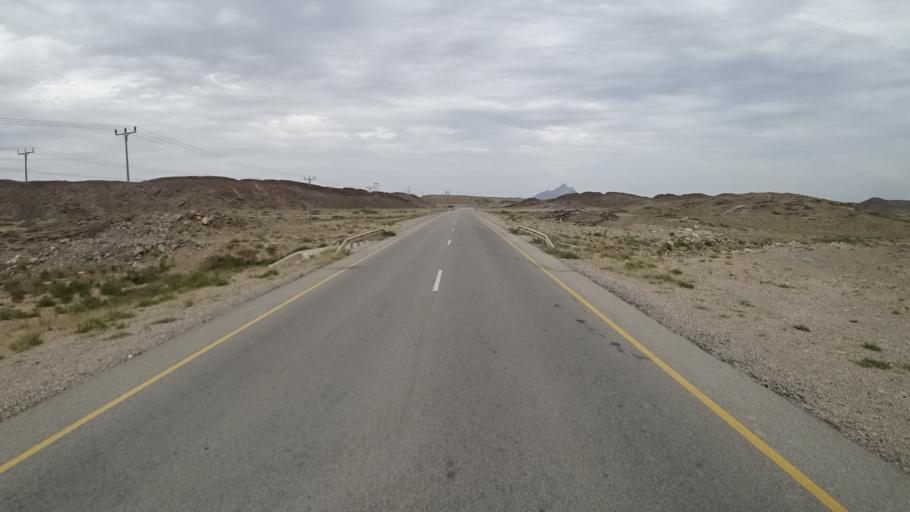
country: OM
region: Zufar
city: Salalah
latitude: 17.0686
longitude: 54.8833
